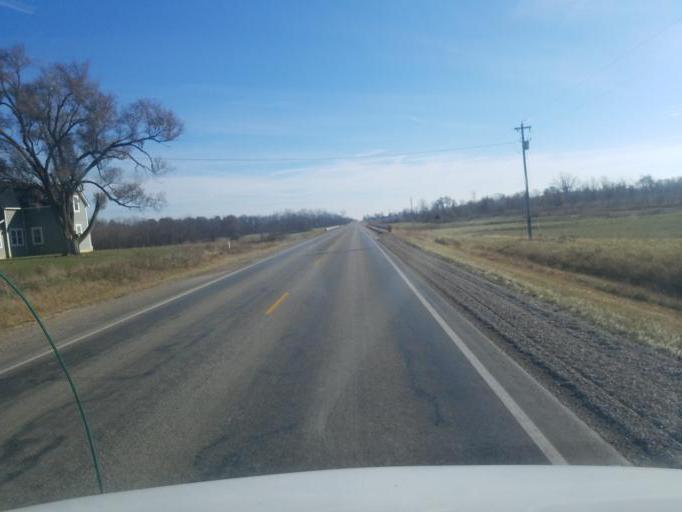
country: US
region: Indiana
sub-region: Adams County
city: Geneva
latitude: 40.5416
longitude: -84.9278
